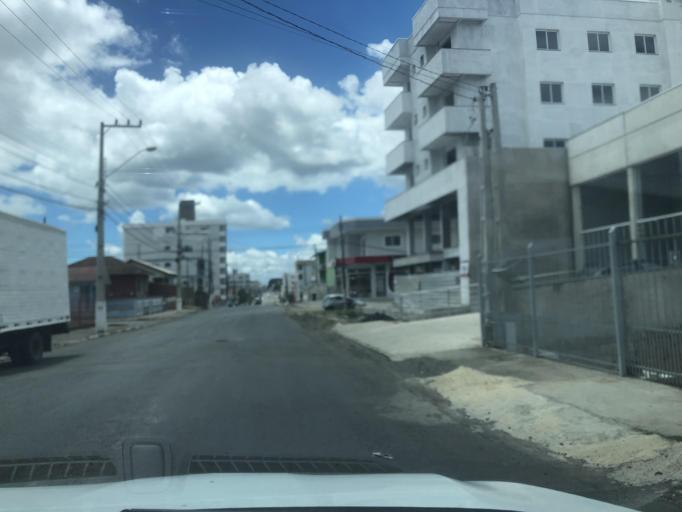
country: BR
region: Santa Catarina
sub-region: Lages
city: Lages
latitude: -27.8085
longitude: -50.3019
